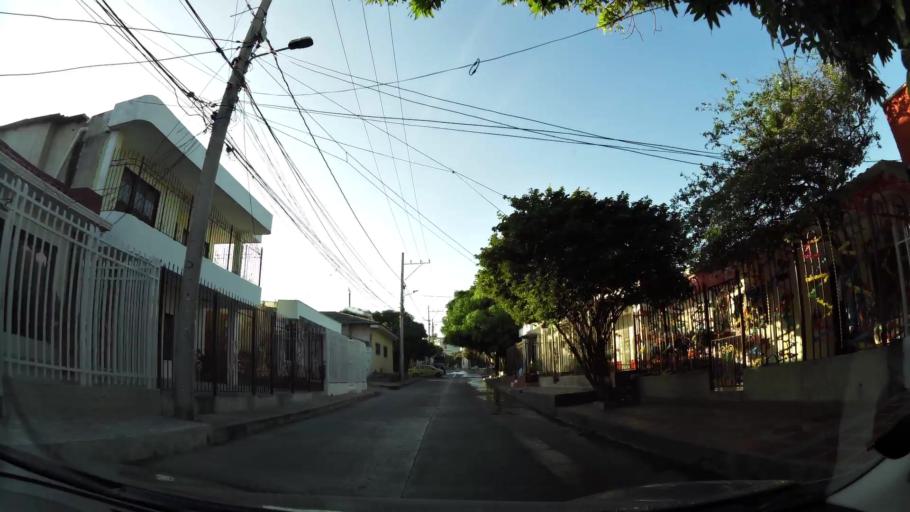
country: CO
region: Atlantico
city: Barranquilla
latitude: 10.9684
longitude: -74.7970
